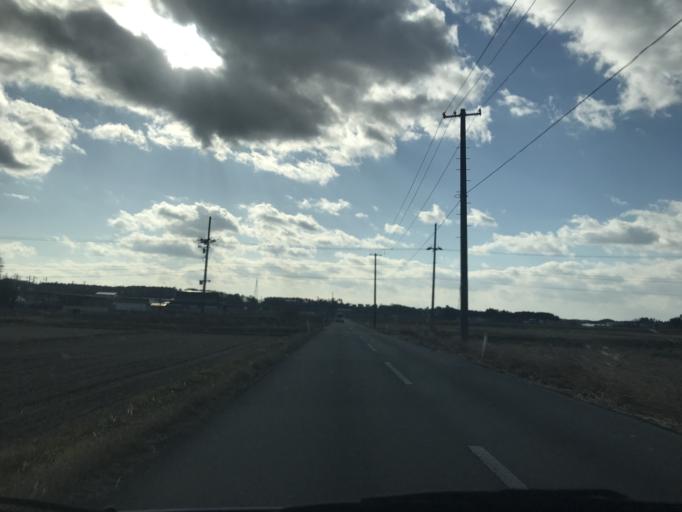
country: JP
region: Iwate
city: Ichinoseki
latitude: 38.7465
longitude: 141.0665
